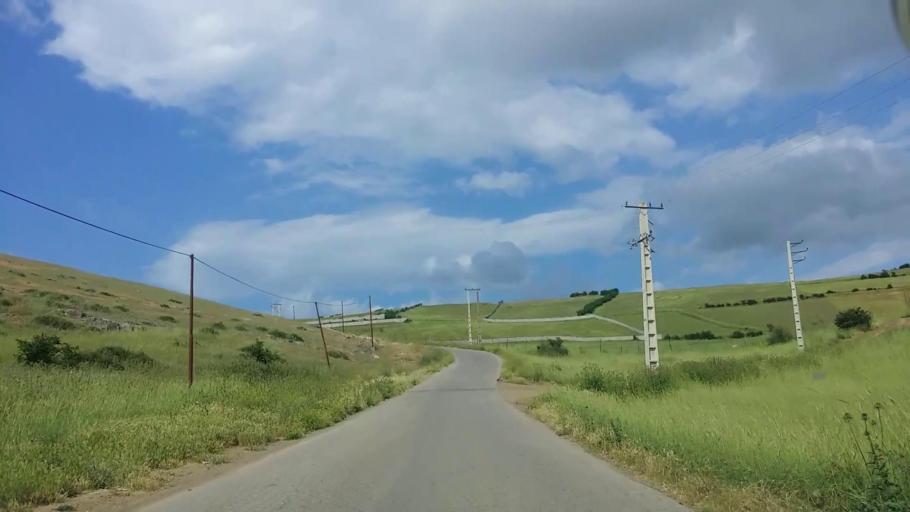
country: IR
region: Mazandaran
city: Chalus
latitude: 36.5264
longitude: 51.2664
